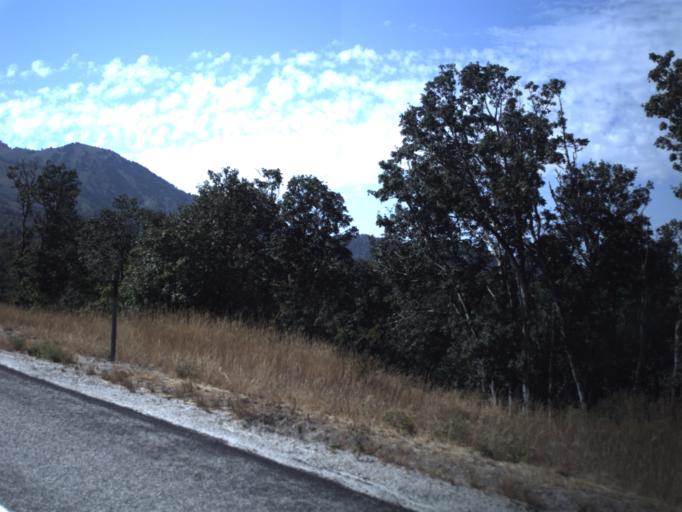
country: US
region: Utah
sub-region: Morgan County
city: Mountain Green
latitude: 41.2056
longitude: -111.8254
